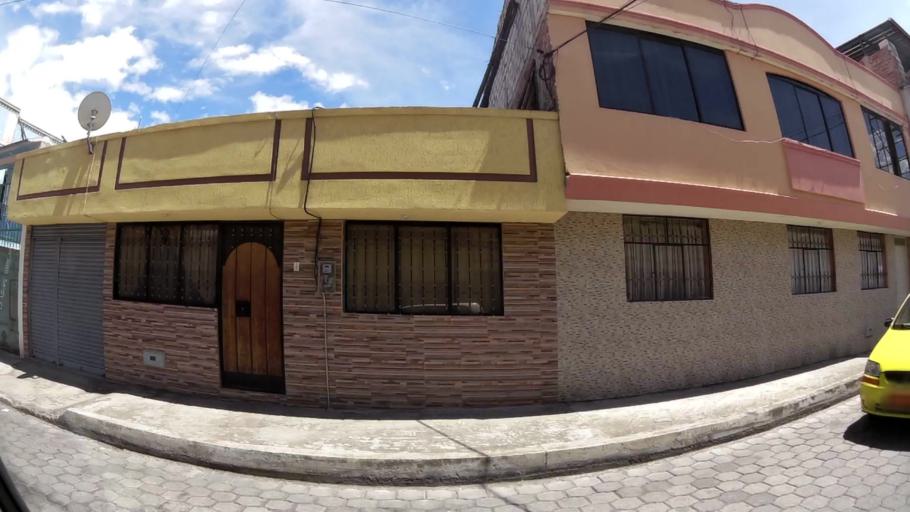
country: EC
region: Chimborazo
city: Riobamba
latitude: -1.6605
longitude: -78.6384
